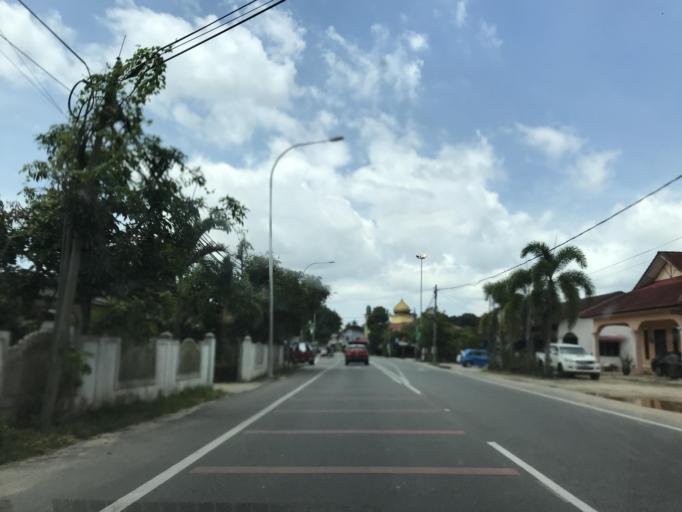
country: MY
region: Kelantan
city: Pasir Mas
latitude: 6.0517
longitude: 102.1867
